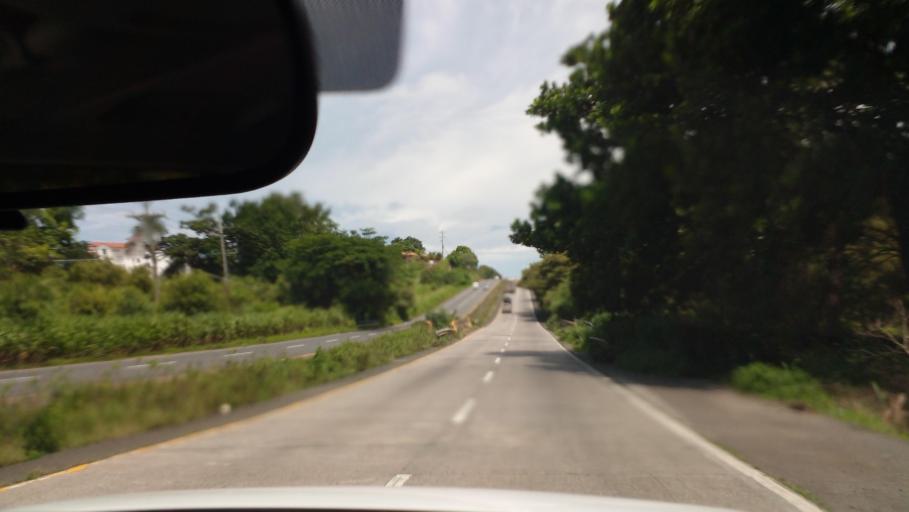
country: PA
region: Panama
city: Nueva Gorgona
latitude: 8.4930
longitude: -79.9582
